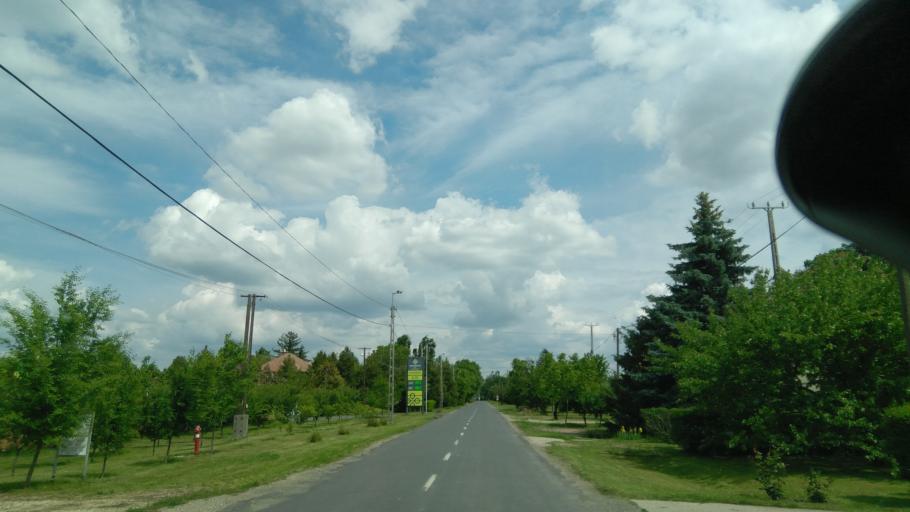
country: HU
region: Bekes
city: Totkomlos
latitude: 46.4120
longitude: 20.7283
